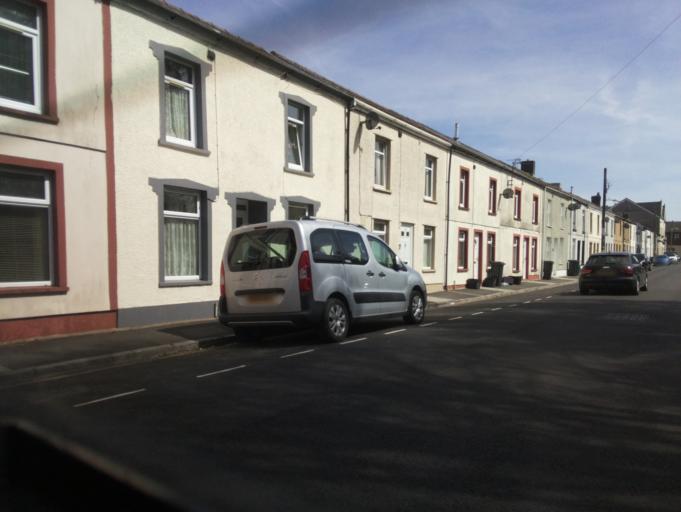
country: GB
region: Wales
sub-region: Merthyr Tydfil County Borough
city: Merthyr Tydfil
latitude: 51.7660
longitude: -3.3518
